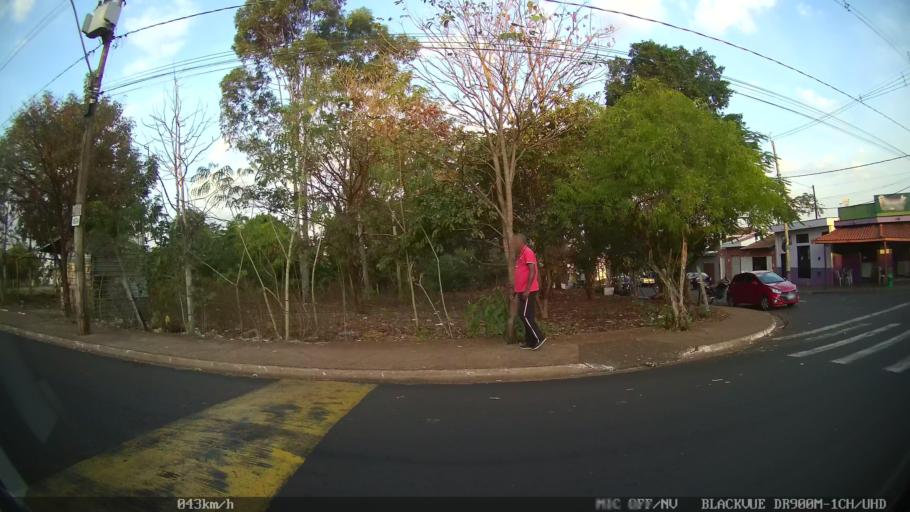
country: BR
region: Sao Paulo
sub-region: Ribeirao Preto
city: Ribeirao Preto
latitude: -21.1248
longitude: -47.8254
